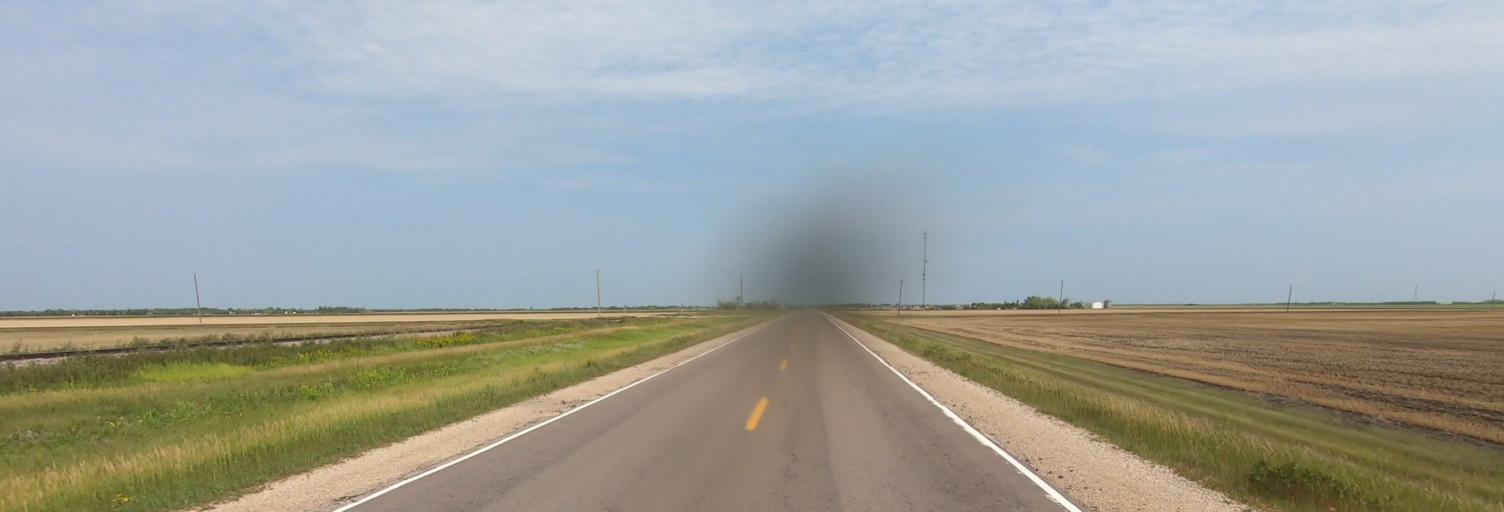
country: CA
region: Manitoba
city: Headingley
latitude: 49.6637
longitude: -97.2853
